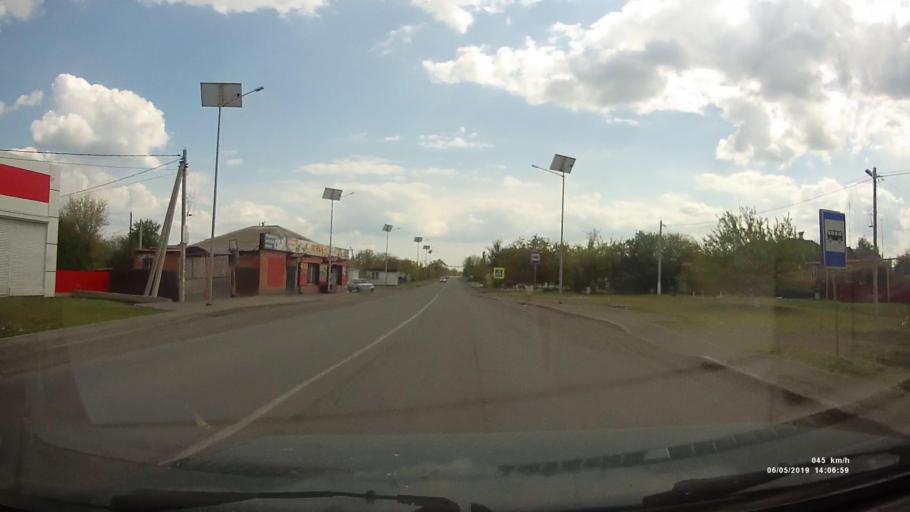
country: RU
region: Rostov
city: Shakhty
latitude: 47.6848
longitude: 40.3005
